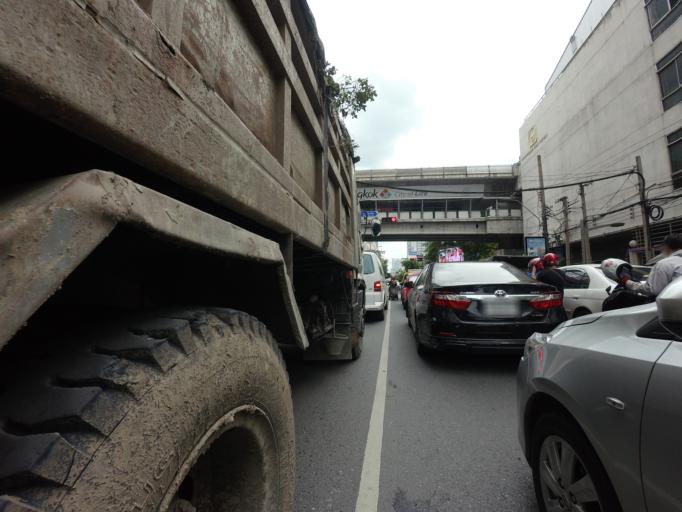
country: TH
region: Bangkok
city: Ratchathewi
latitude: 13.7438
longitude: 100.5426
